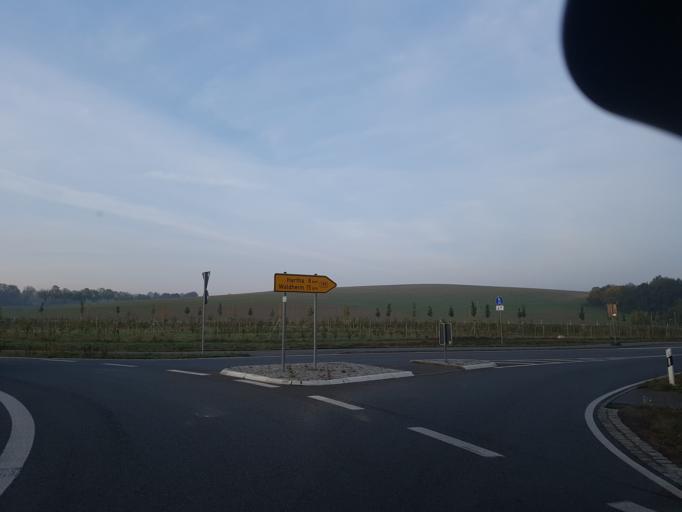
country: DE
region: Saxony
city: Grossweitzschen
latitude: 51.1265
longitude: 13.0546
